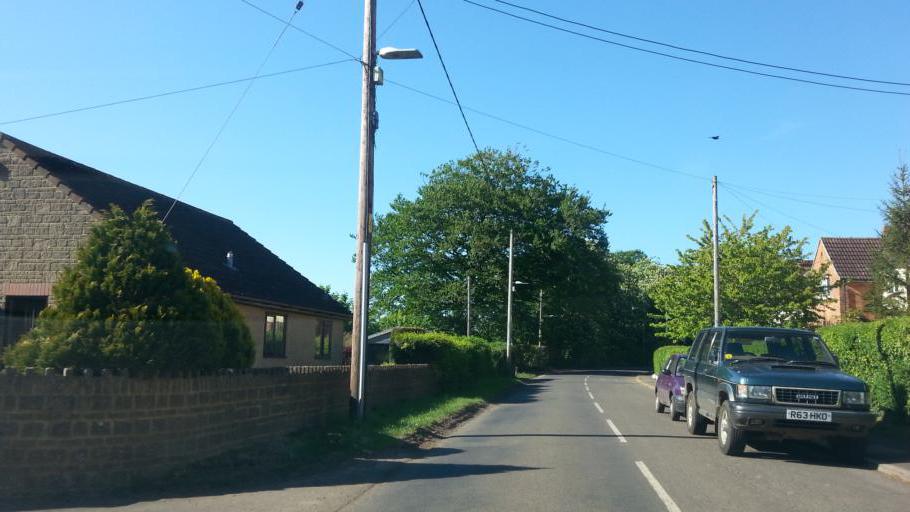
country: GB
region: England
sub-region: Somerset
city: Milborne Port
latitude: 50.9729
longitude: -2.4620
